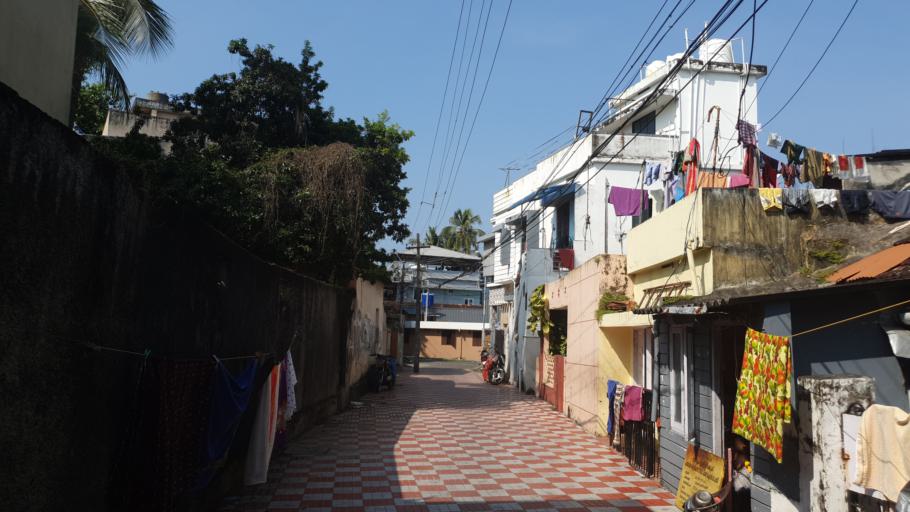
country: IN
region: Kerala
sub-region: Ernakulam
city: Cochin
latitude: 9.9596
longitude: 76.2562
